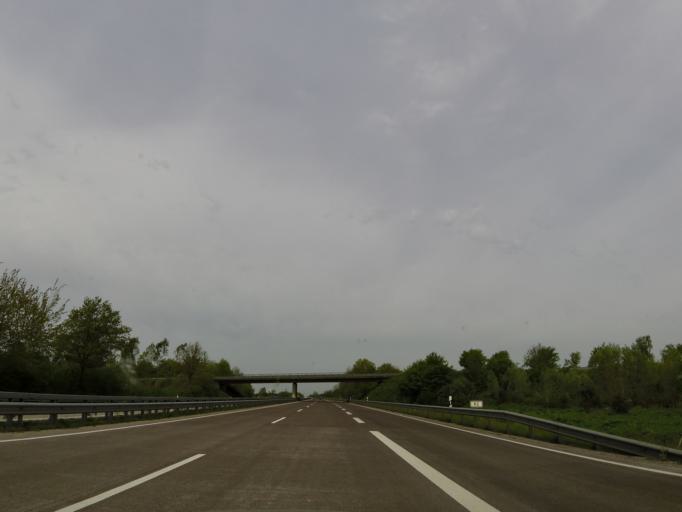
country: DE
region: Schleswig-Holstein
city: Klein Offenseth-Sparrieshoop
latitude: 53.8062
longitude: 9.6776
